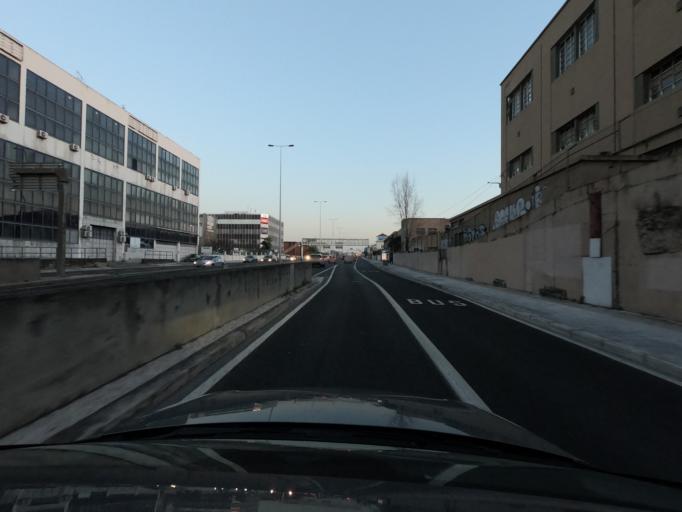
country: PT
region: Lisbon
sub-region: Loures
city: Moscavide
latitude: 38.7612
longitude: -9.1037
